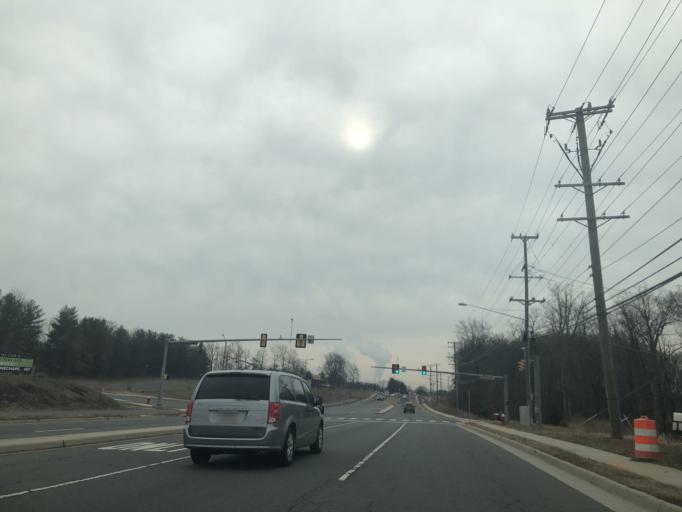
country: US
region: Virginia
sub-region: Loudoun County
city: Leesburg
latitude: 39.0876
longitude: -77.5534
